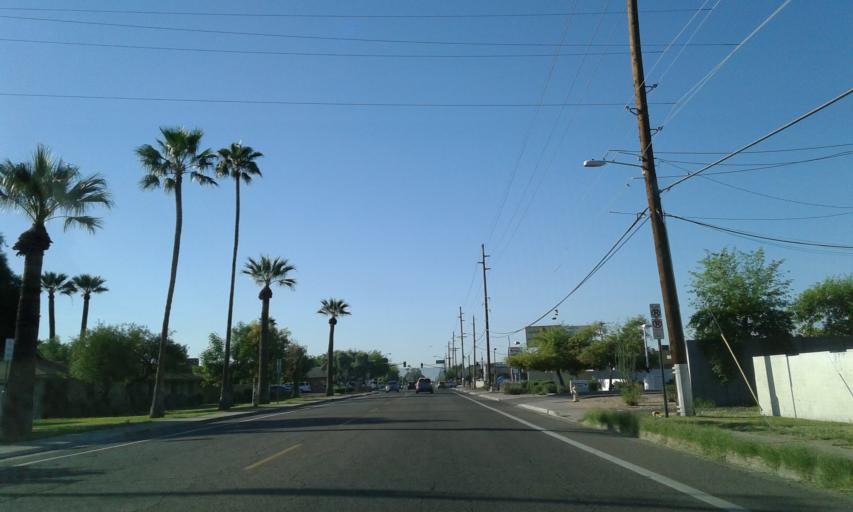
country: US
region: Arizona
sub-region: Maricopa County
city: Glendale
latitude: 33.5261
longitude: -112.1083
